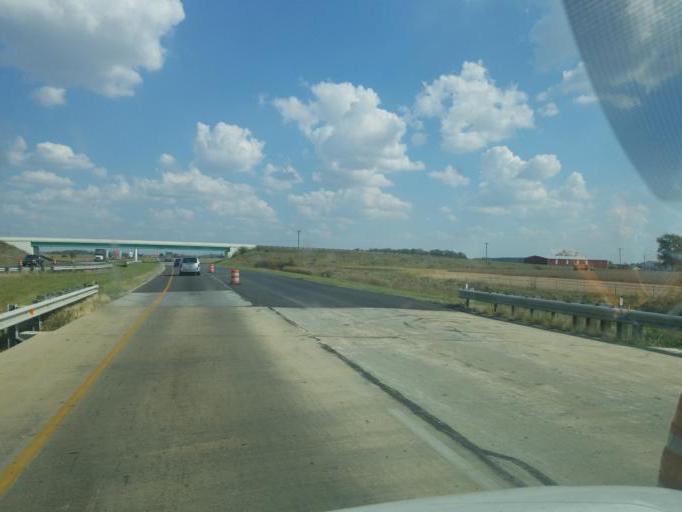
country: US
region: Ohio
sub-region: Van Wert County
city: Van Wert
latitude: 40.8698
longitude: -84.5070
